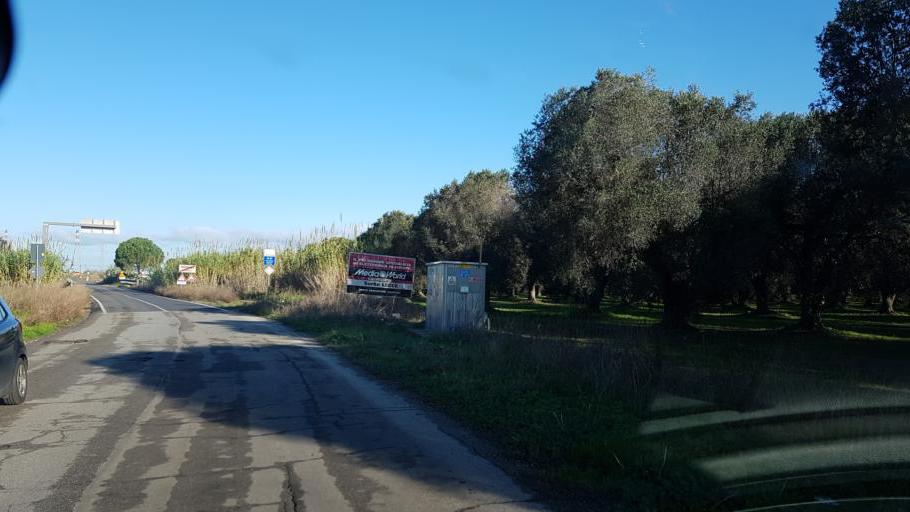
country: IT
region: Apulia
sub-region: Provincia di Brindisi
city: Tuturano
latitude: 40.5491
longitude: 17.9475
